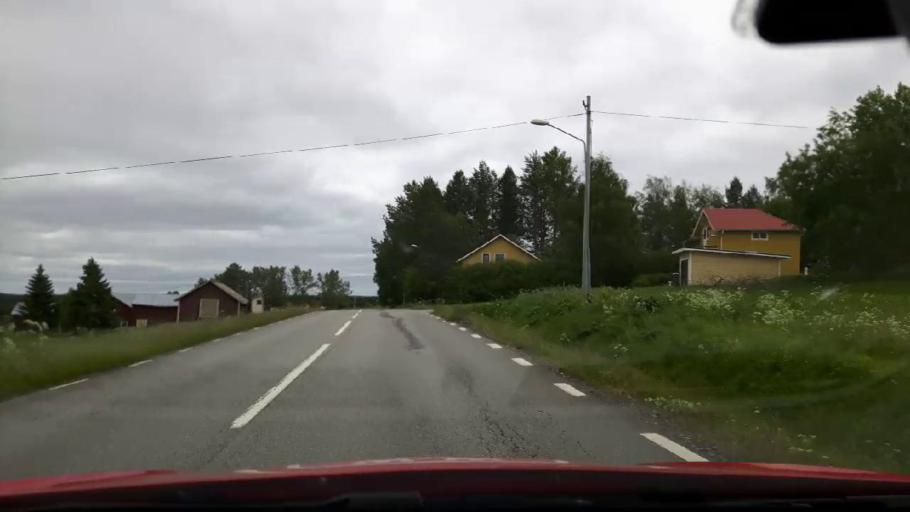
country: SE
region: Jaemtland
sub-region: Stroemsunds Kommun
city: Stroemsund
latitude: 63.5610
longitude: 15.3984
